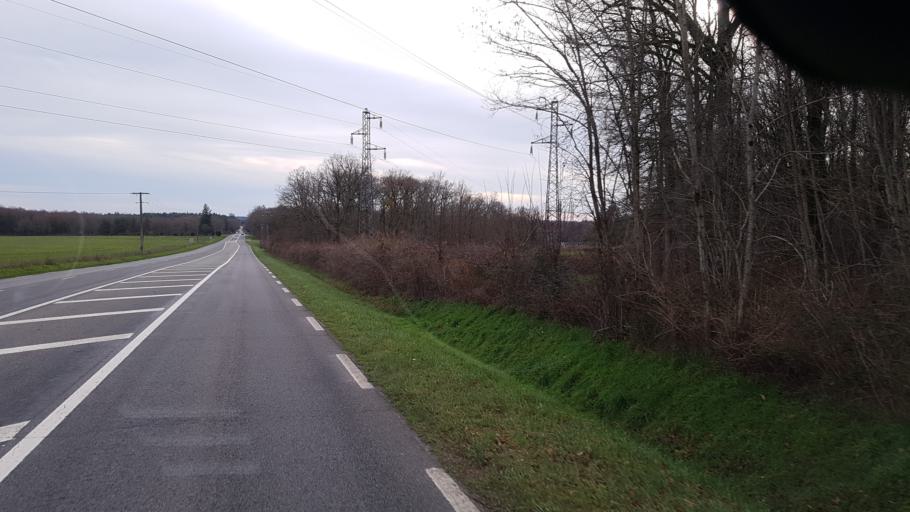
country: FR
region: Centre
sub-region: Departement du Loir-et-Cher
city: Nouan-le-Fuzelier
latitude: 47.5590
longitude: 2.0322
